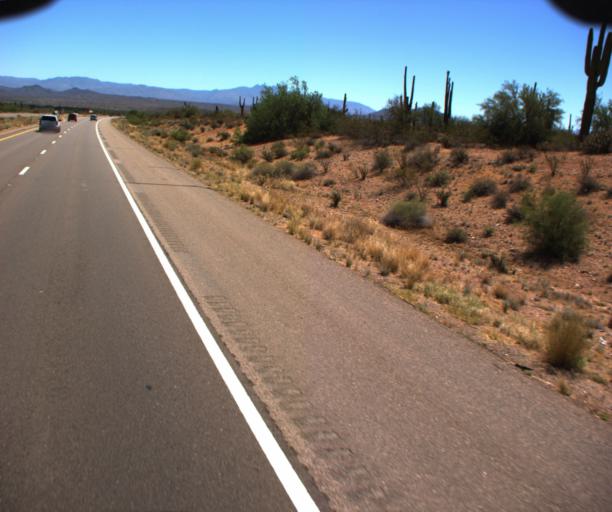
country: US
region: Arizona
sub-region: Maricopa County
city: Fountain Hills
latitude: 33.5734
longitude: -111.6955
